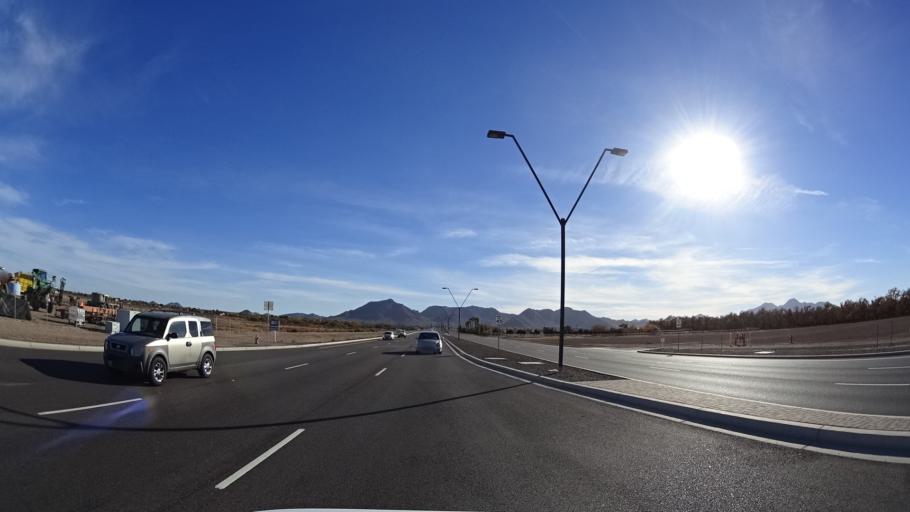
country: US
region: Arizona
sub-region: Maricopa County
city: Queen Creek
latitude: 33.2262
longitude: -111.6346
